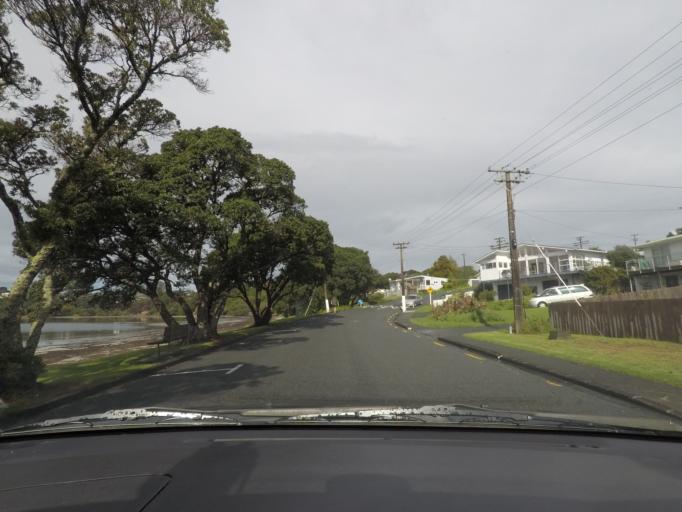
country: NZ
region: Auckland
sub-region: Auckland
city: Warkworth
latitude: -36.4223
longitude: 174.7308
